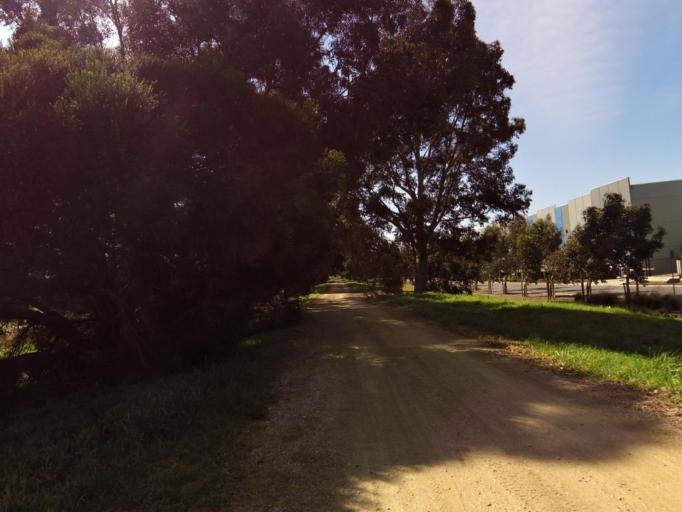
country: AU
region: Victoria
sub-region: Greater Dandenong
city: Keysborough
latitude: -38.0146
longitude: 145.1900
